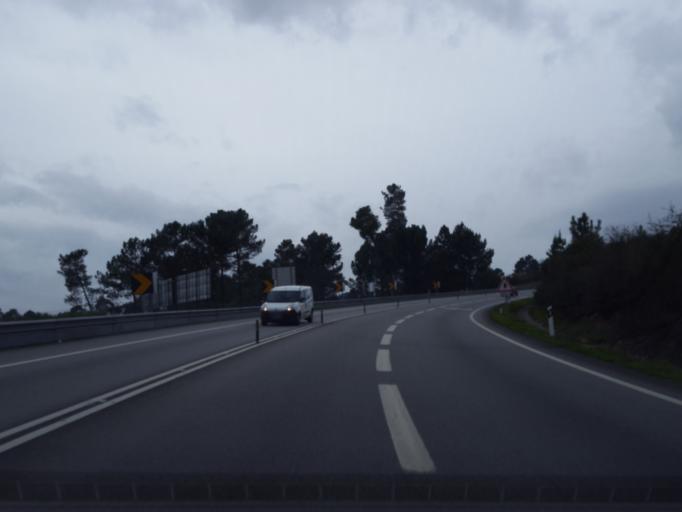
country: PT
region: Porto
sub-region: Marco de Canaveses
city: Marco de Canavezes
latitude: 41.2063
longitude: -8.1651
